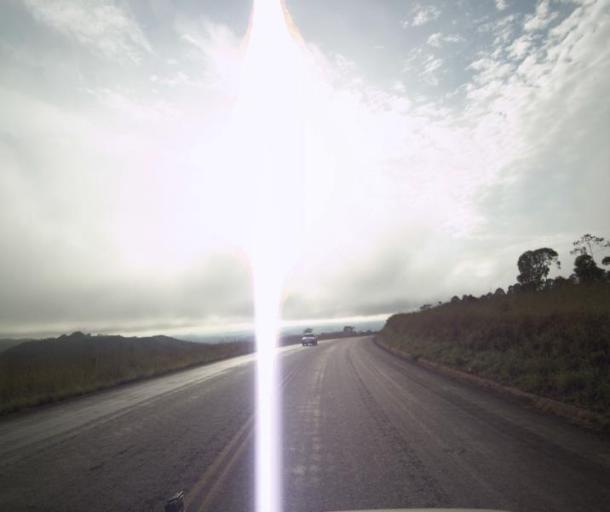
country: BR
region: Goias
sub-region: Pirenopolis
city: Pirenopolis
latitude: -15.7528
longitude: -48.7481
